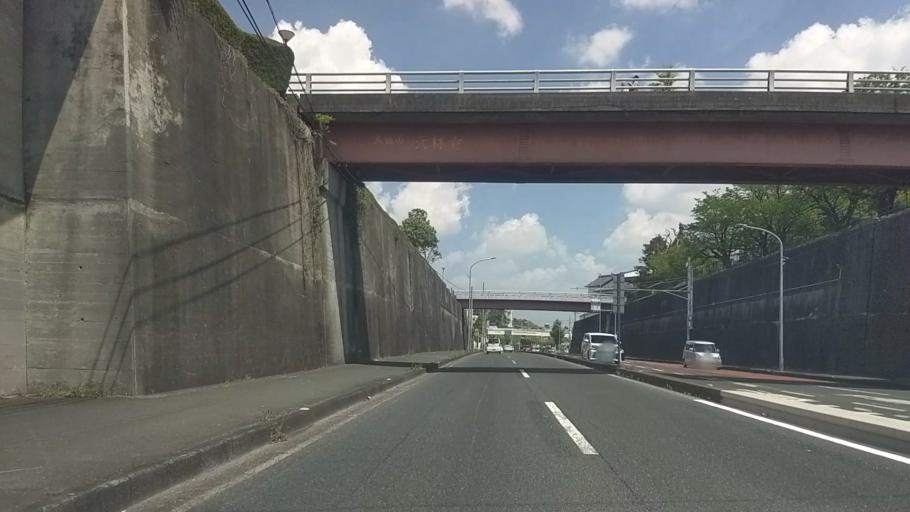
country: JP
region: Shizuoka
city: Hamamatsu
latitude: 34.7158
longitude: 137.7284
